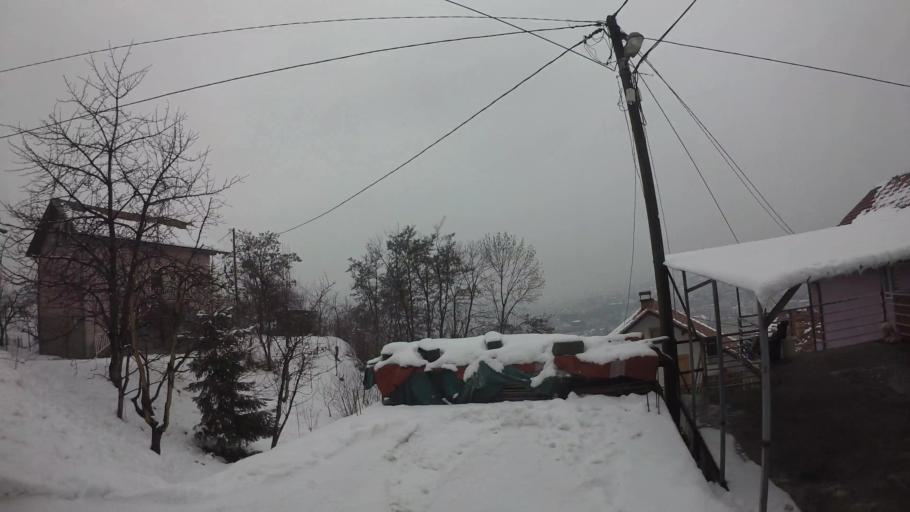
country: BA
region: Federation of Bosnia and Herzegovina
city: Kobilja Glava
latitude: 43.8524
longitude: 18.4195
